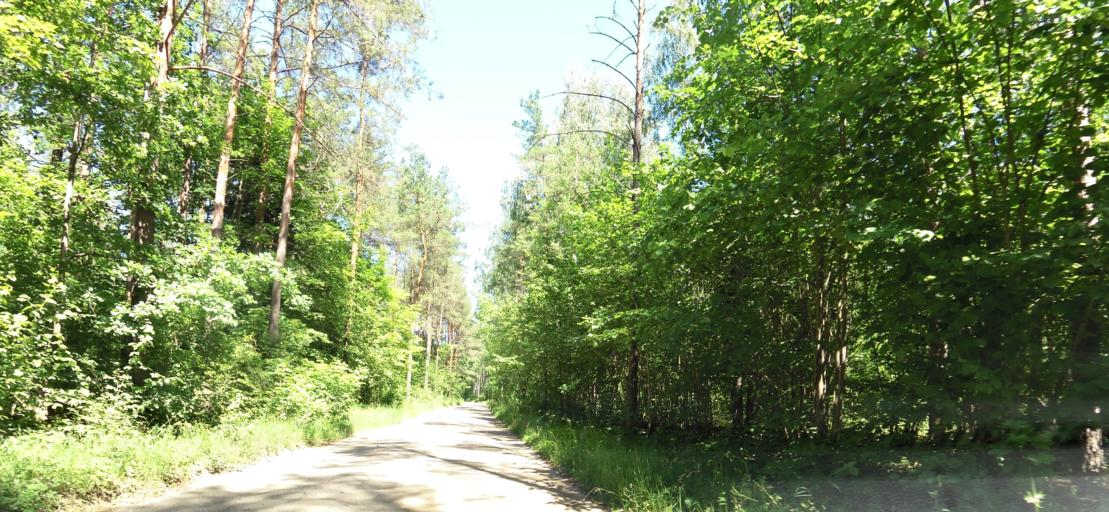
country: LT
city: Grigiskes
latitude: 54.7927
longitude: 24.9752
